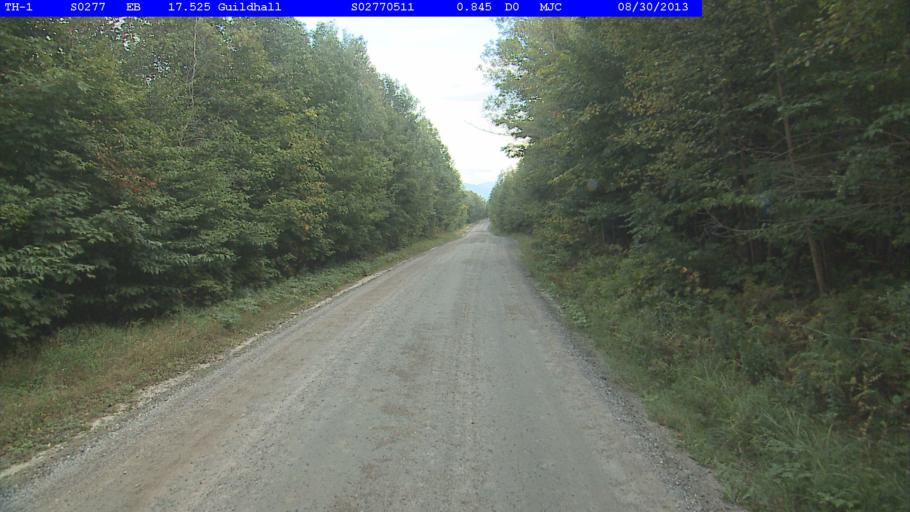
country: US
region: Vermont
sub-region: Essex County
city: Guildhall
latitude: 44.5714
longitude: -71.6533
